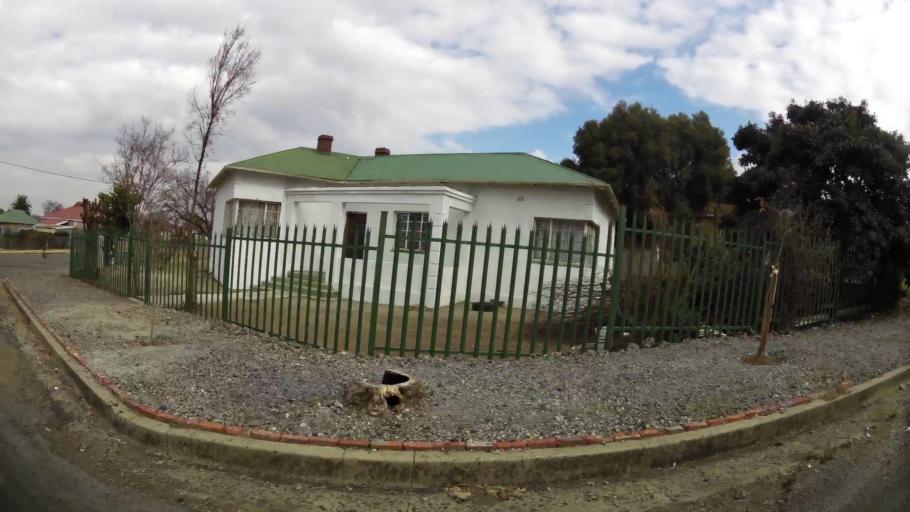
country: ZA
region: Orange Free State
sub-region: Fezile Dabi District Municipality
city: Kroonstad
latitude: -27.6529
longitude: 27.2355
